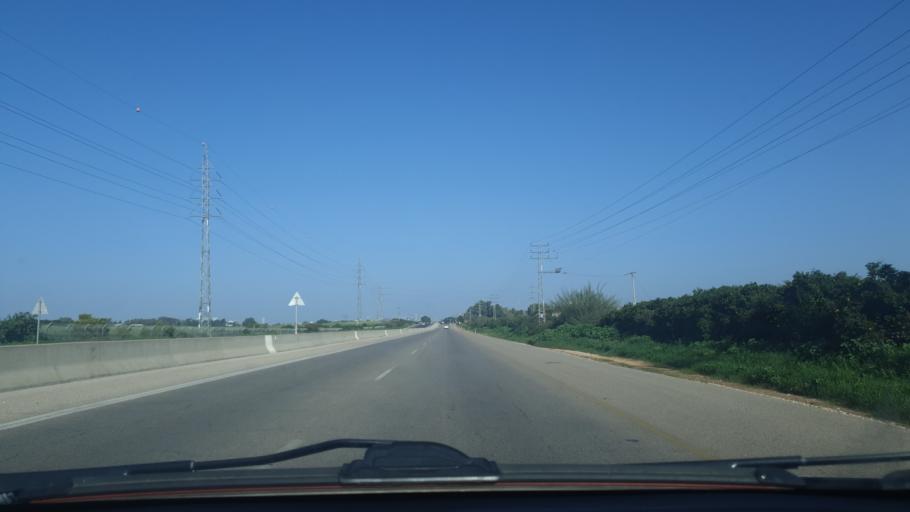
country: IL
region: Central District
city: Kefar Habad
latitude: 31.9810
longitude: 34.8353
